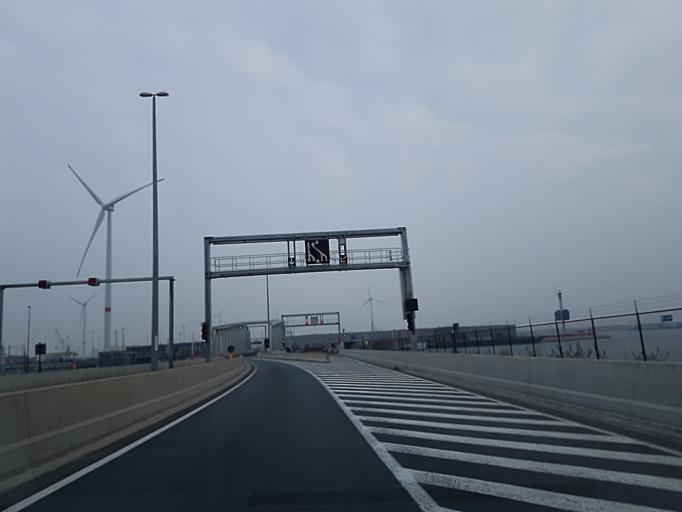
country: BE
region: Flanders
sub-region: Provincie Oost-Vlaanderen
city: Beveren
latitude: 51.2774
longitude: 4.2428
